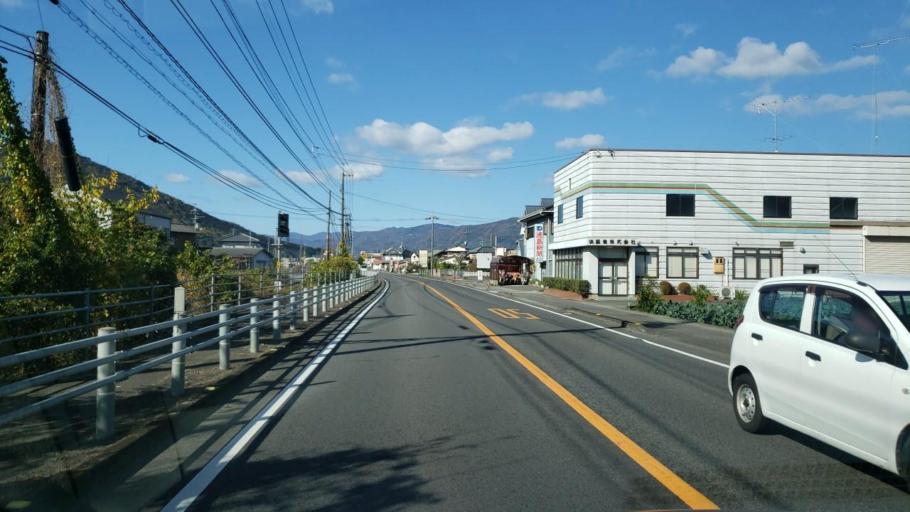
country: JP
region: Tokushima
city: Wakimachi
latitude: 34.0596
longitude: 134.2166
